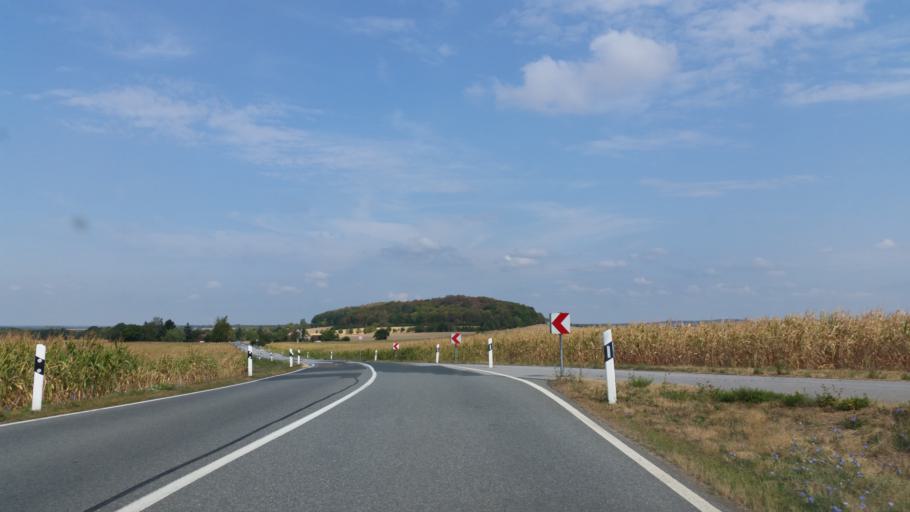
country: DE
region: Saxony
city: Weissenberg
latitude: 51.1659
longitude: 14.6573
